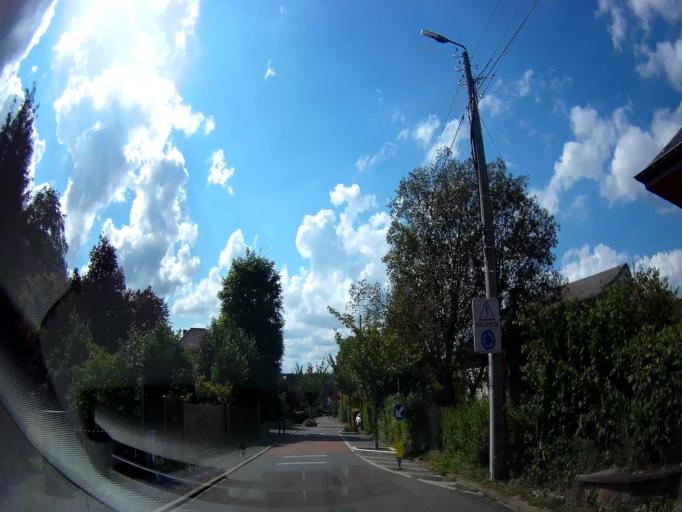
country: BE
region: Wallonia
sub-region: Province de Namur
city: Yvoir
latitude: 50.3482
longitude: 4.8753
